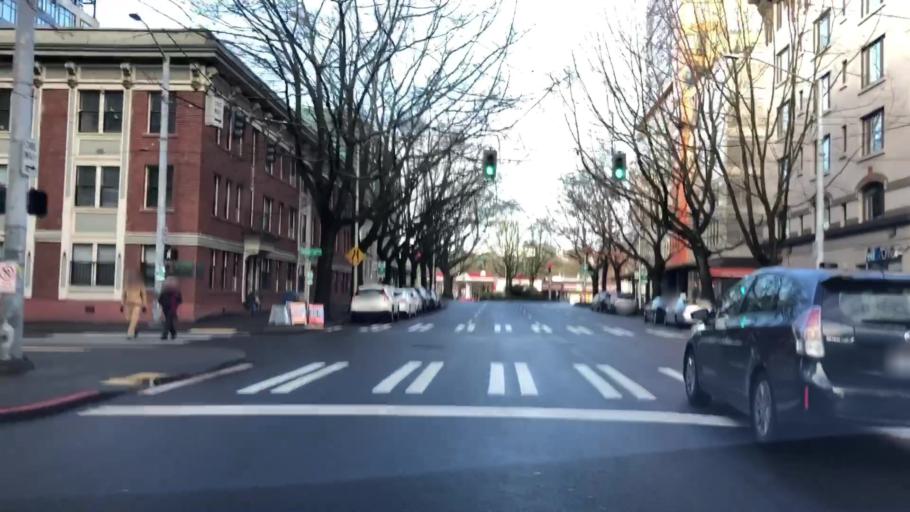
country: US
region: Washington
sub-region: King County
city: Seattle
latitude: 47.6177
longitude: -122.3479
